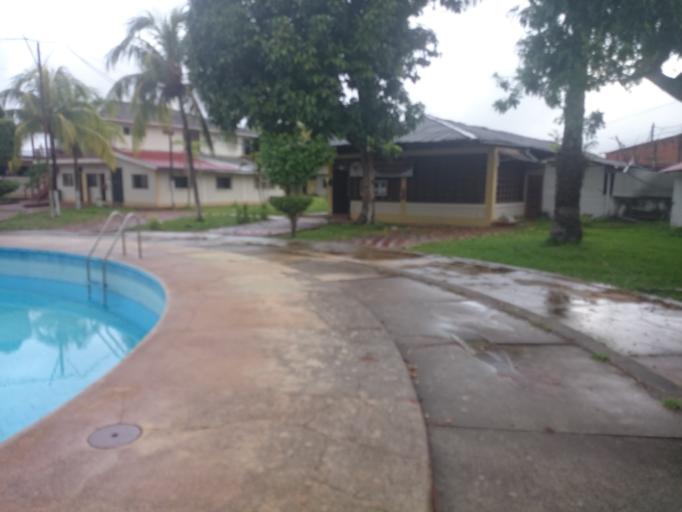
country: PE
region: Ucayali
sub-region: Provincia de Coronel Portillo
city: Puerto Callao
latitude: -8.3709
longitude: -74.5666
